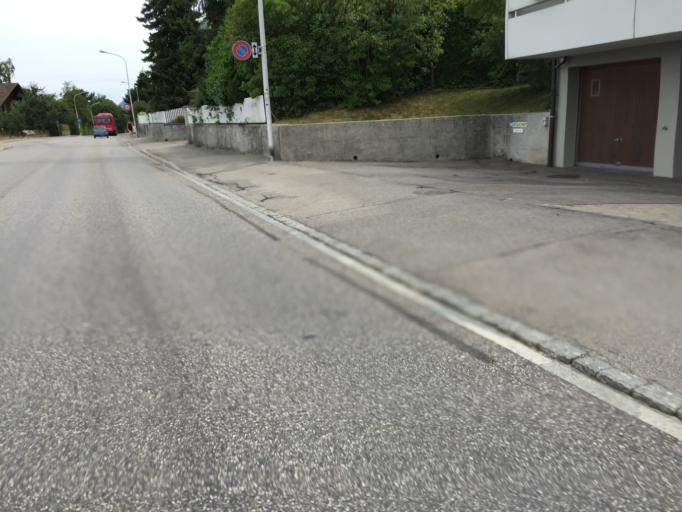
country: CH
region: Bern
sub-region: Bern-Mittelland District
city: Koniz
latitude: 46.9242
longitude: 7.4302
